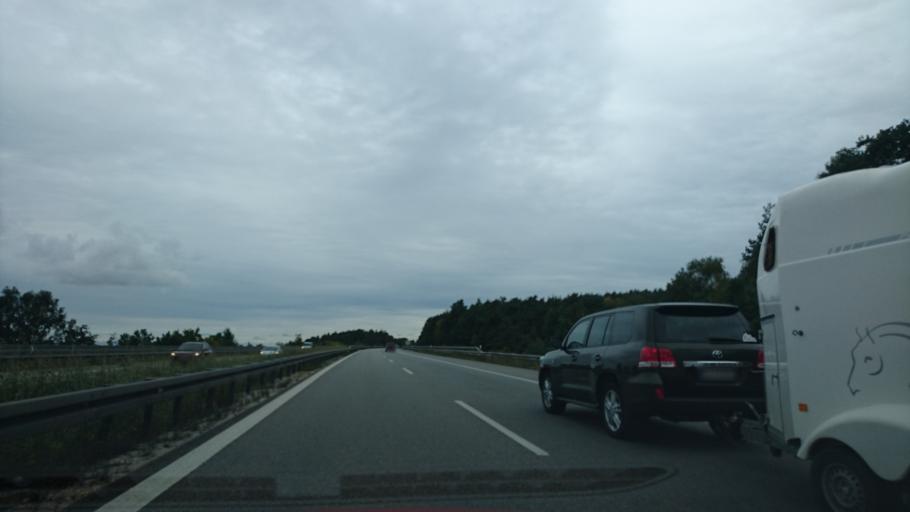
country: DE
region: Bavaria
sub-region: Upper Palatinate
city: Maxhutte-Haidhof
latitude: 49.1922
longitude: 12.1196
